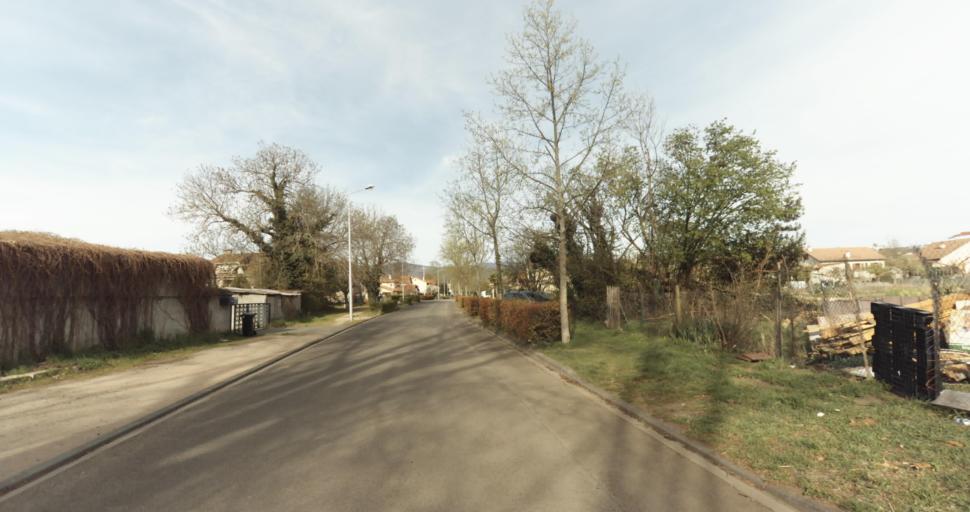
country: FR
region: Auvergne
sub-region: Departement du Puy-de-Dome
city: Cebazat
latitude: 45.8315
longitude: 3.1106
